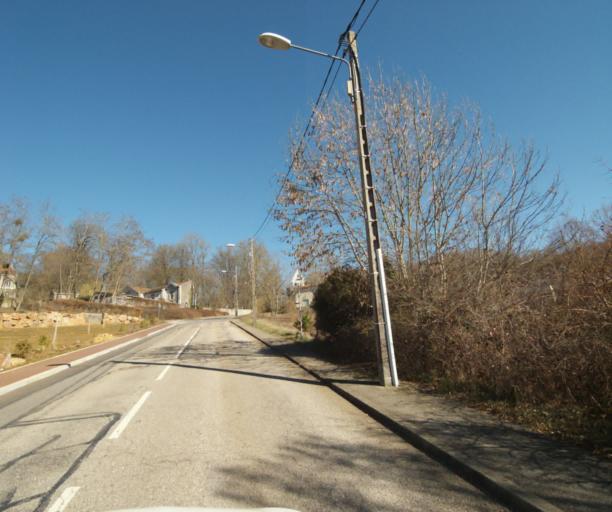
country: FR
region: Lorraine
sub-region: Departement de Meurthe-et-Moselle
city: Essey-les-Nancy
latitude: 48.7170
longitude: 6.2199
